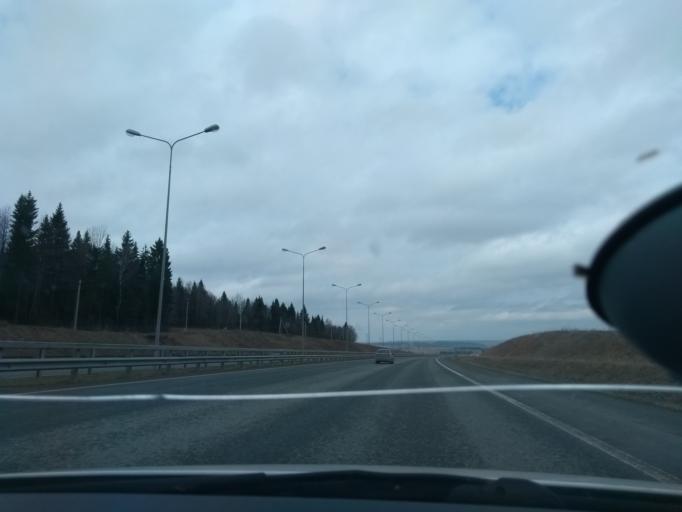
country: RU
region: Perm
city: Zvezdnyy
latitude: 57.7624
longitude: 56.3334
